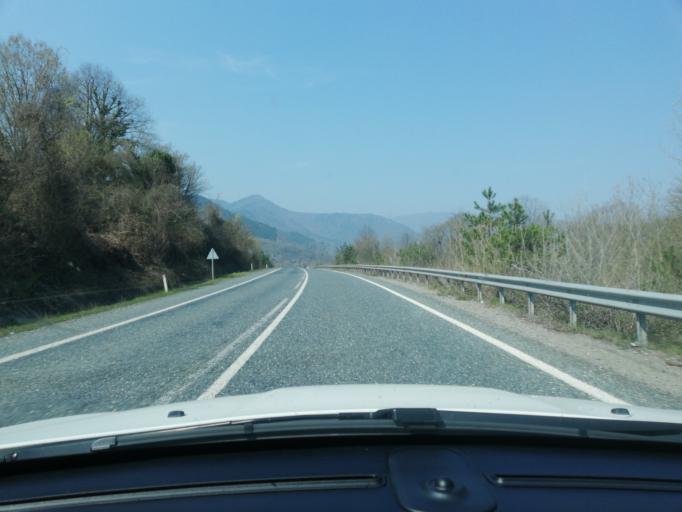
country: TR
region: Zonguldak
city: Gokcebey
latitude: 41.2289
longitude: 32.2029
